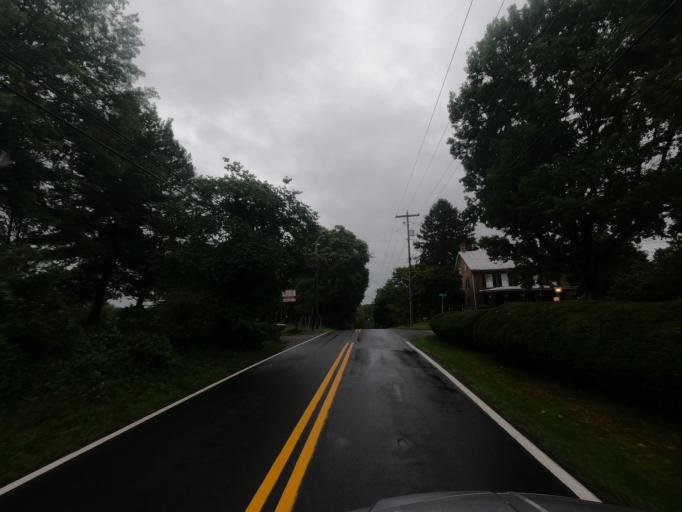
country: US
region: Maryland
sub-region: Washington County
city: Wilson-Conococheague
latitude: 39.6286
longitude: -77.9407
